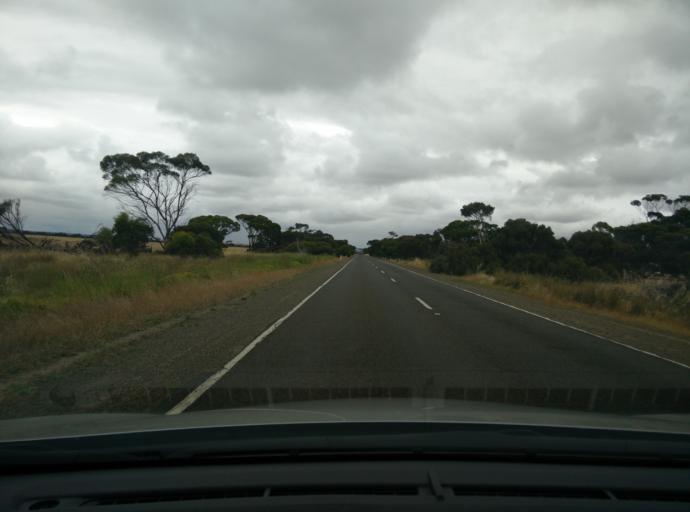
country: AU
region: South Australia
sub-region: Kangaroo Island
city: Kingscote
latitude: -35.6888
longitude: 137.5720
